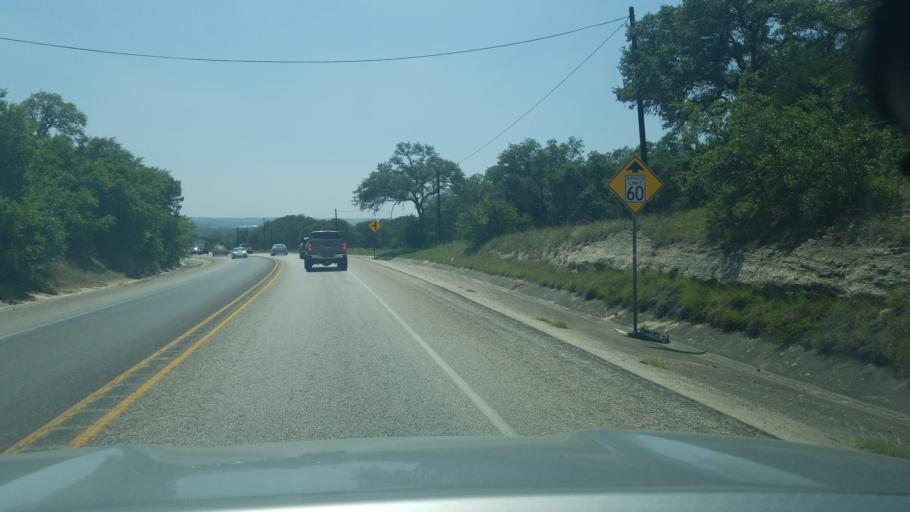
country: US
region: Texas
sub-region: Kendall County
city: Boerne
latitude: 29.7887
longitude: -98.6856
